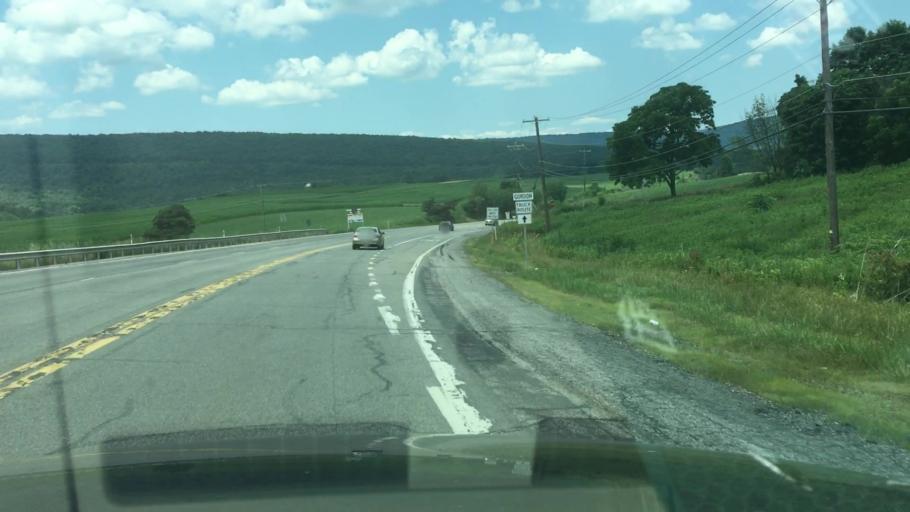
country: US
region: Pennsylvania
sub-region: Schuylkill County
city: Ashland
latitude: 40.7265
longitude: -76.3911
